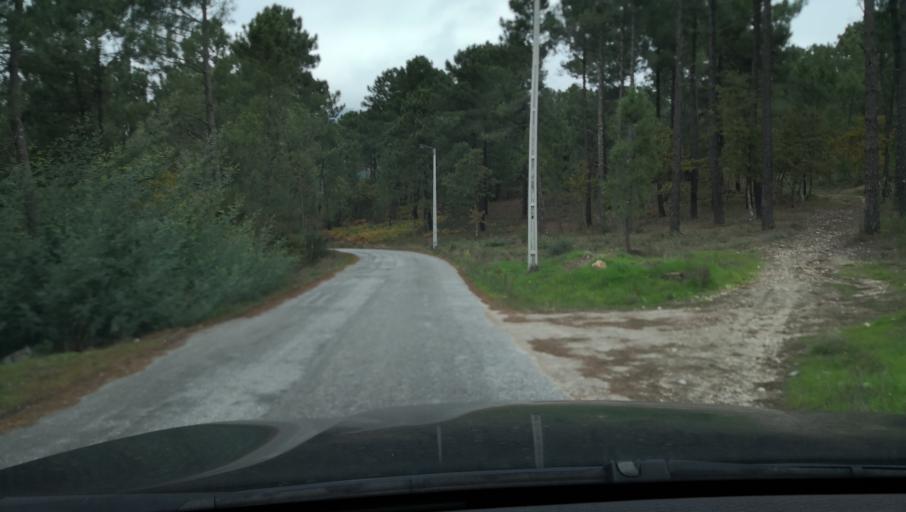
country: PT
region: Vila Real
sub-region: Vila Real
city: Vila Real
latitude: 41.3193
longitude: -7.7535
